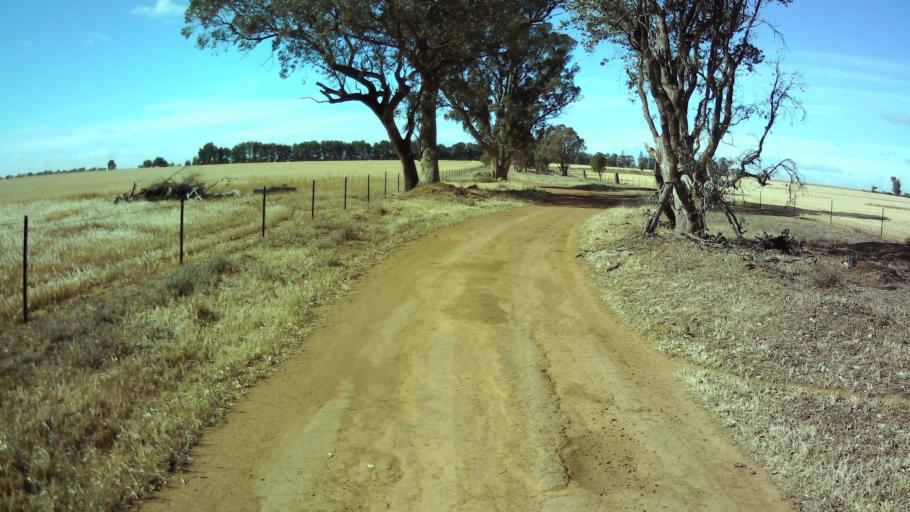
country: AU
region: New South Wales
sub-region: Weddin
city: Grenfell
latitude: -34.0557
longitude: 148.2681
